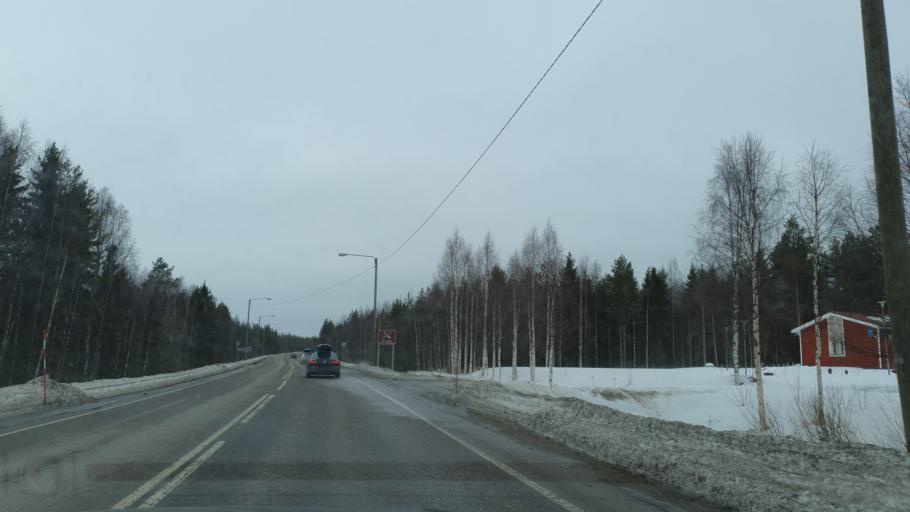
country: FI
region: Lapland
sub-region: Torniolaakso
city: Pello
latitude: 66.8249
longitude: 24.0031
